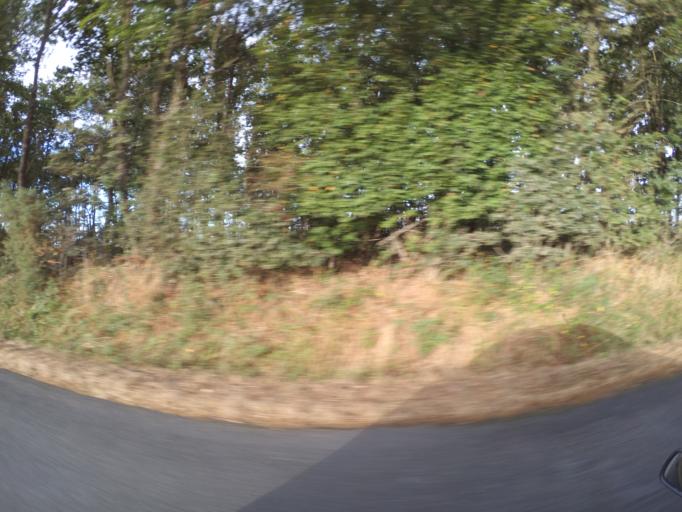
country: FR
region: Pays de la Loire
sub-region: Departement de la Loire-Atlantique
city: Vieillevigne
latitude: 46.9943
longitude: -1.4611
